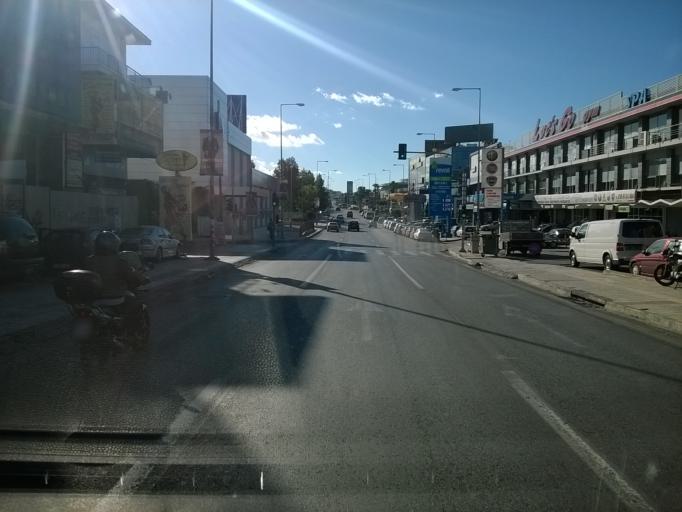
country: GR
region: Attica
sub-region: Nomarchia Athinas
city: Dhafni
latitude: 37.9423
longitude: 23.7400
